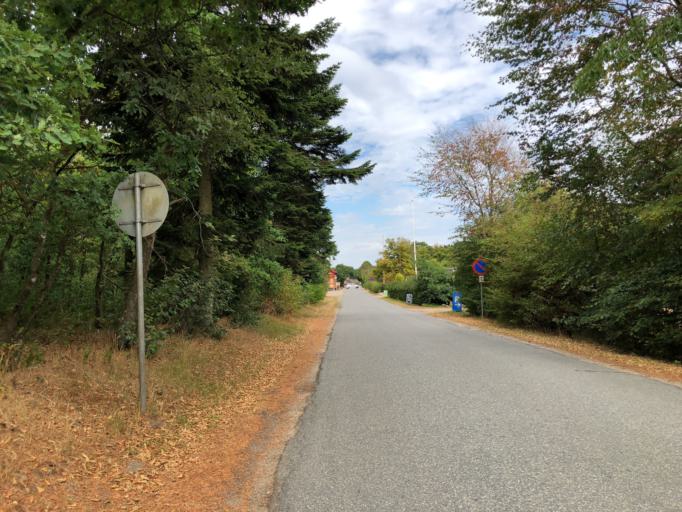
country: DK
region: South Denmark
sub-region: Vejle Kommune
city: Egtved
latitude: 55.6555
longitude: 9.2612
